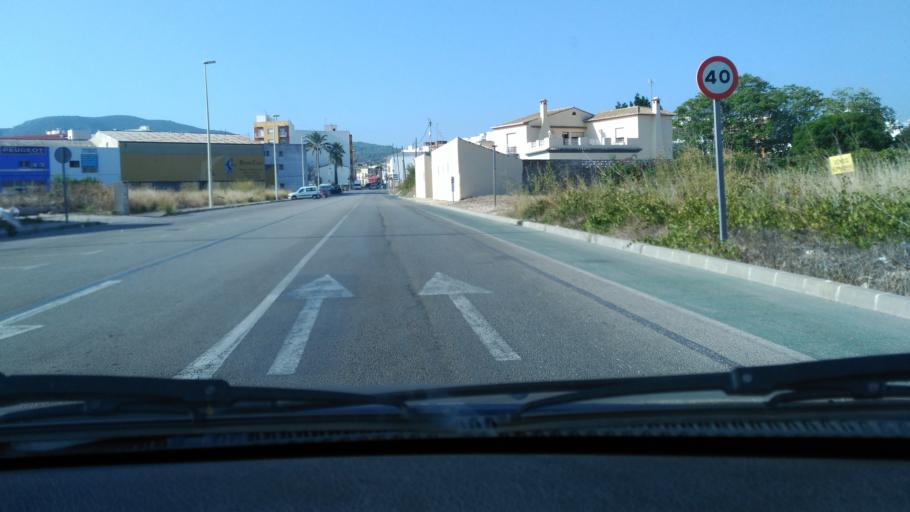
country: ES
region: Valencia
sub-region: Provincia de Alicante
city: Gata de Gorgos
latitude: 38.7792
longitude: 0.0866
